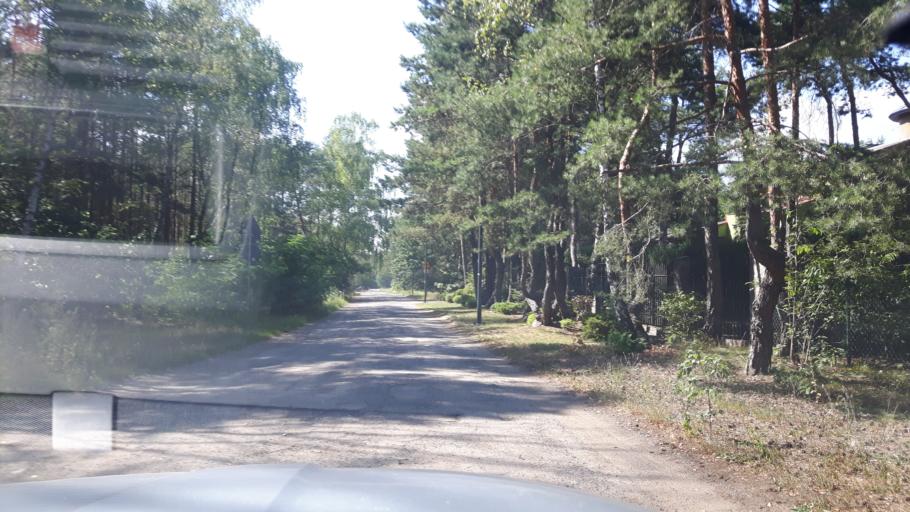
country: PL
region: Masovian Voivodeship
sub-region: Warszawa
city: Wesola
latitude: 52.2426
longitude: 21.2137
